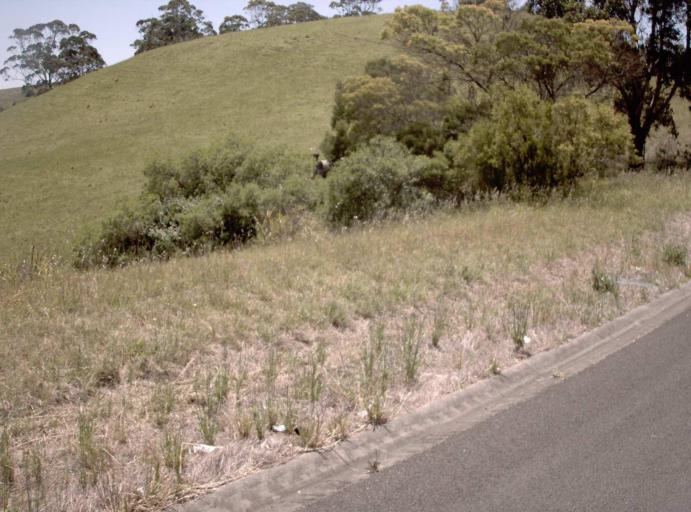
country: AU
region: Victoria
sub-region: East Gippsland
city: Lakes Entrance
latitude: -37.8530
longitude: 148.0366
